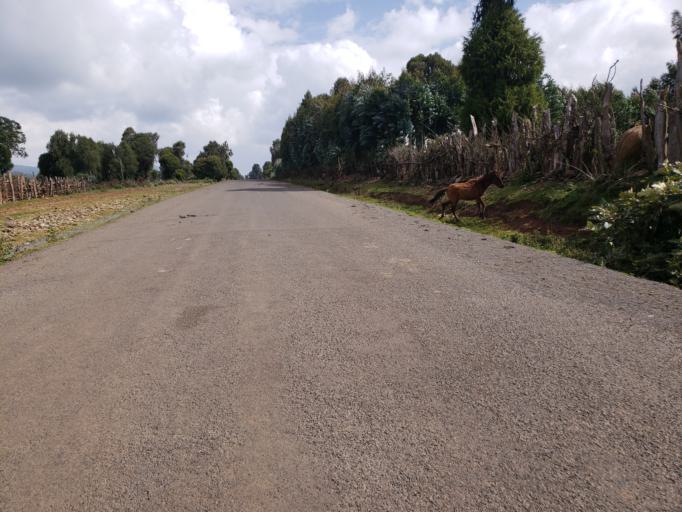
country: ET
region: Oromiya
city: Dodola
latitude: 6.8683
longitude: 39.3890
